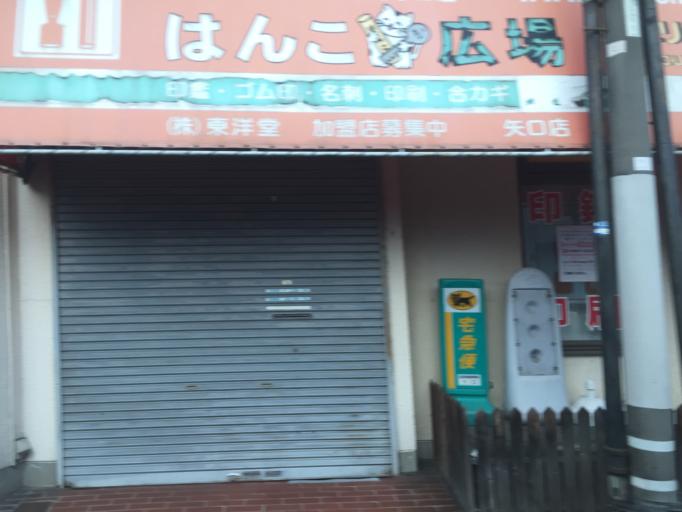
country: JP
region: Kanagawa
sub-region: Kawasaki-shi
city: Kawasaki
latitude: 35.5625
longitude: 139.6916
